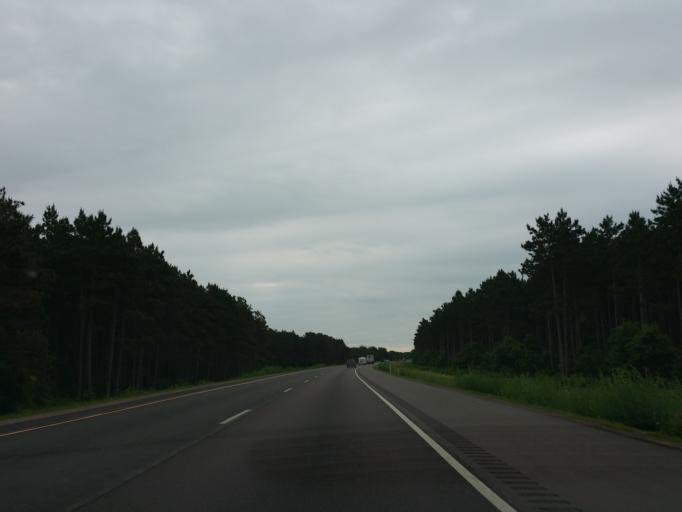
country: US
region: Wisconsin
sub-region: Trempealeau County
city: Osseo
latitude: 44.5634
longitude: -91.1859
